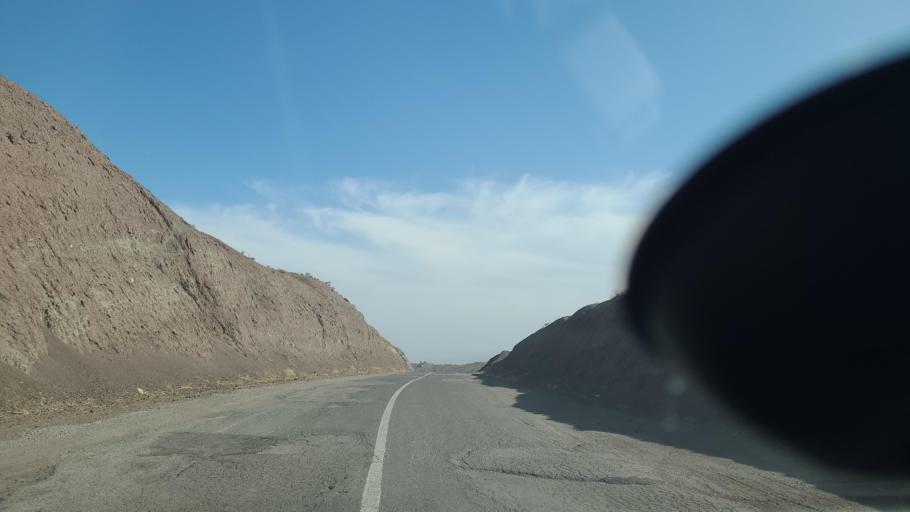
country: IR
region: Razavi Khorasan
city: Fariman
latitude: 35.5940
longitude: 59.7170
